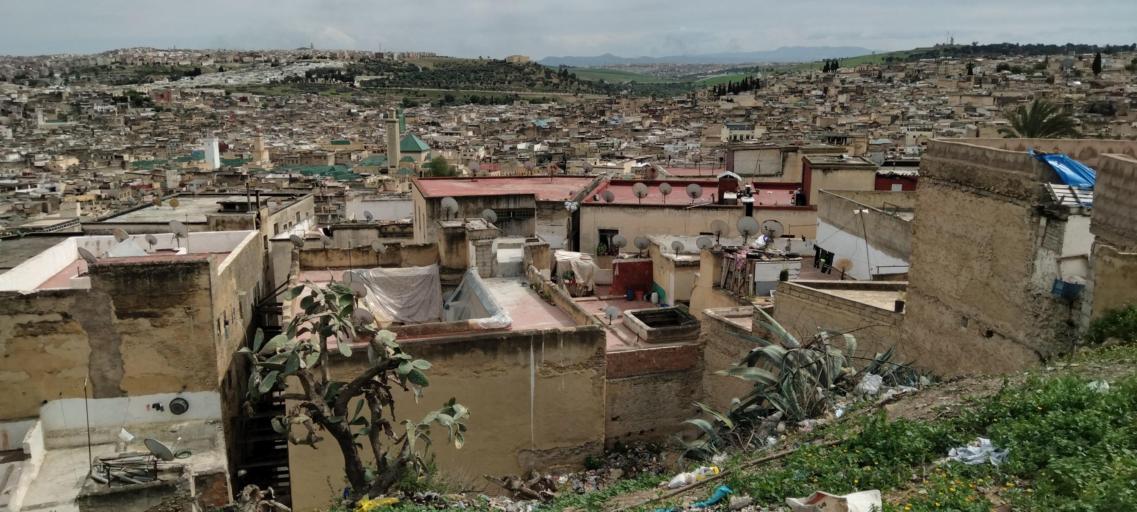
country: MA
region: Fes-Boulemane
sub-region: Fes
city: Fes
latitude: 34.0682
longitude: -4.9771
